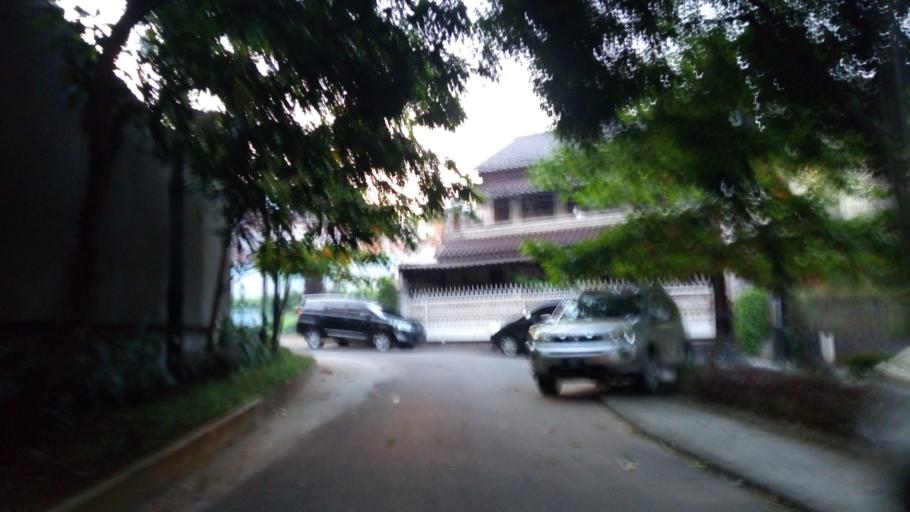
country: ID
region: Jakarta Raya
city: Jakarta
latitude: -6.2425
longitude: 106.7952
